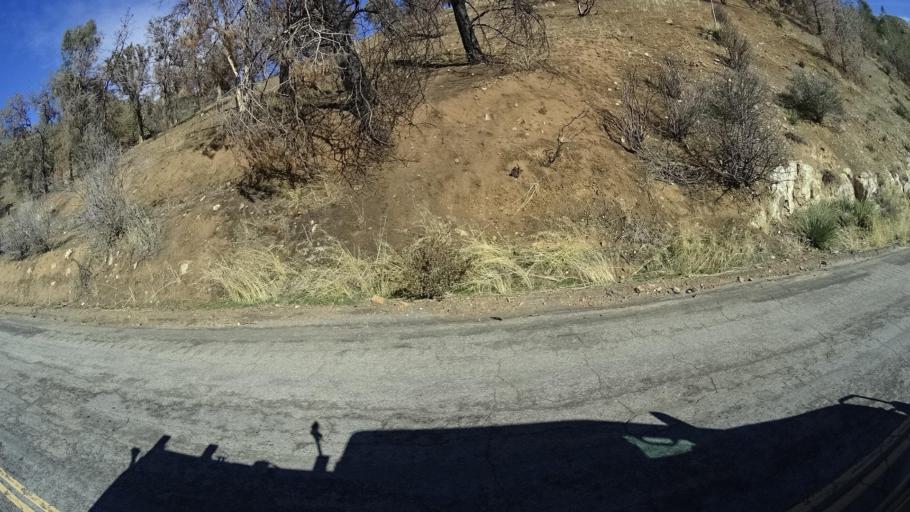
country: US
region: California
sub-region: Kern County
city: Bodfish
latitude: 35.4561
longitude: -118.5294
